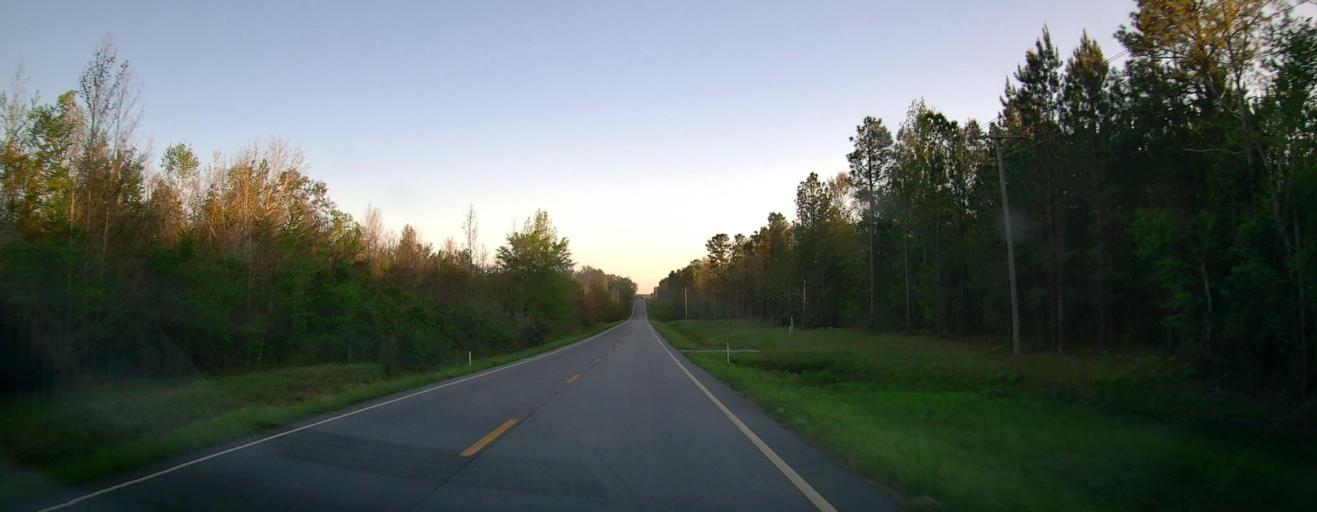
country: US
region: Georgia
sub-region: Talbot County
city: Talbotton
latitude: 32.5523
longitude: -84.5695
